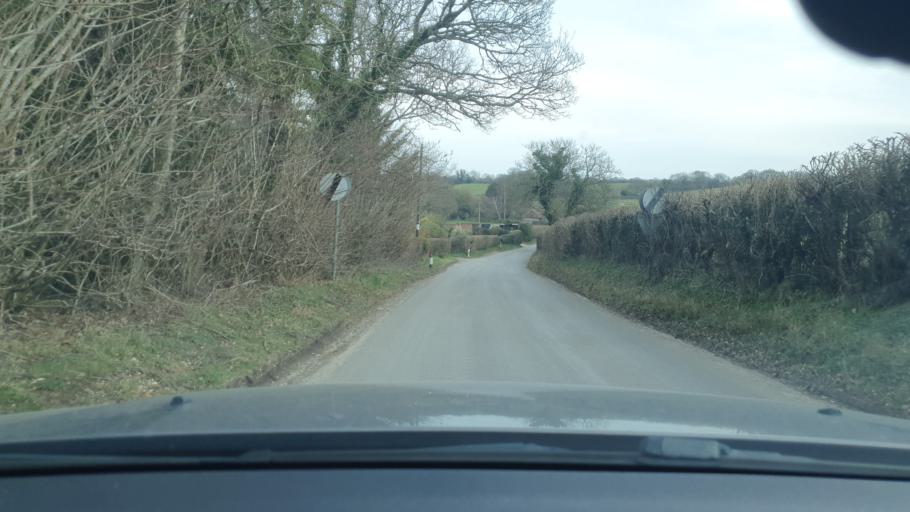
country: GB
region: England
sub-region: West Berkshire
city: Kintbury
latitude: 51.3721
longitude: -1.4824
